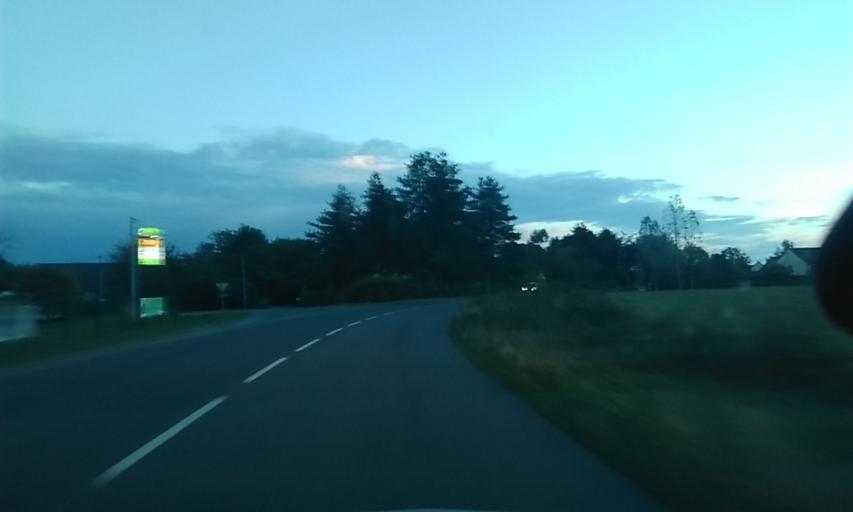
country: FR
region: Brittany
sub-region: Departement d'Ille-et-Vilaine
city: Saint-Thurial
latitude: 48.0414
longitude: -1.9278
